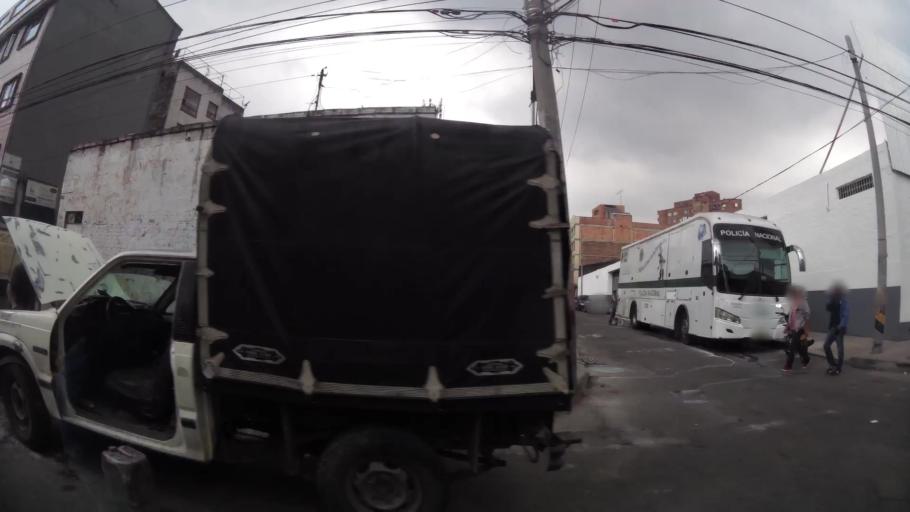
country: CO
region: Bogota D.C.
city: Bogota
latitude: 4.5961
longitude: -74.0868
